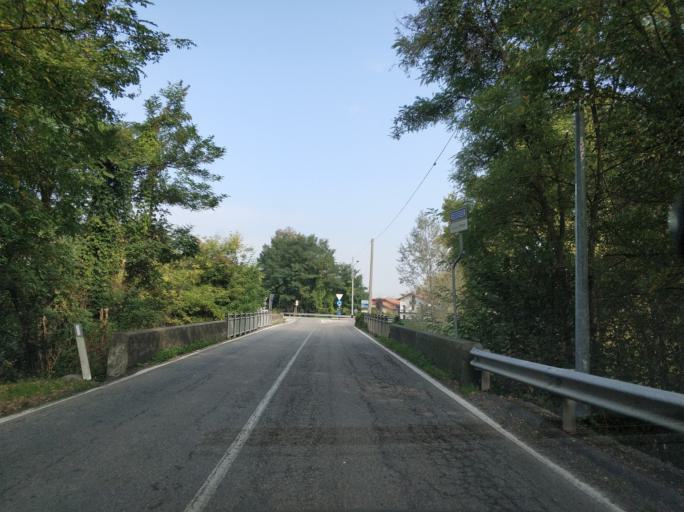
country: IT
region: Piedmont
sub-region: Provincia di Biella
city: Ceresane-Curanuova
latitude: 45.5148
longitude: 8.0055
